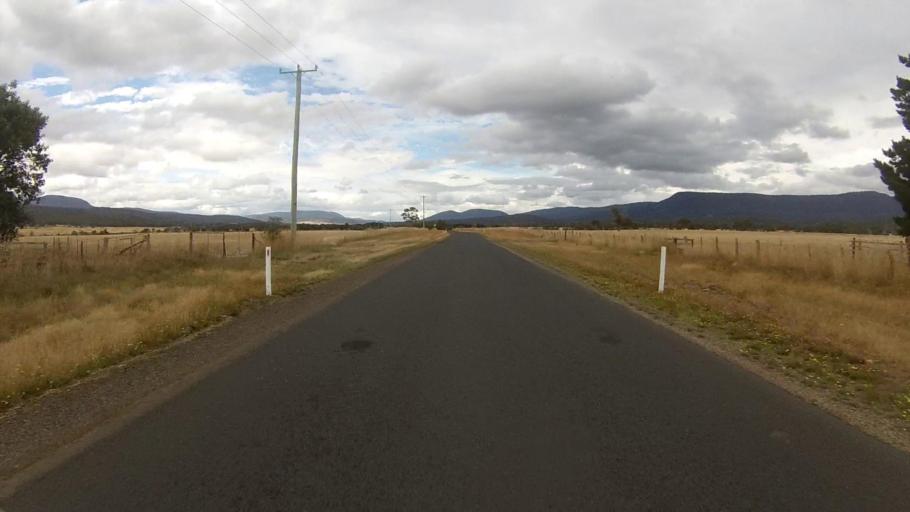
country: AU
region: Tasmania
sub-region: Northern Midlands
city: Evandale
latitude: -41.8248
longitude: 147.8377
